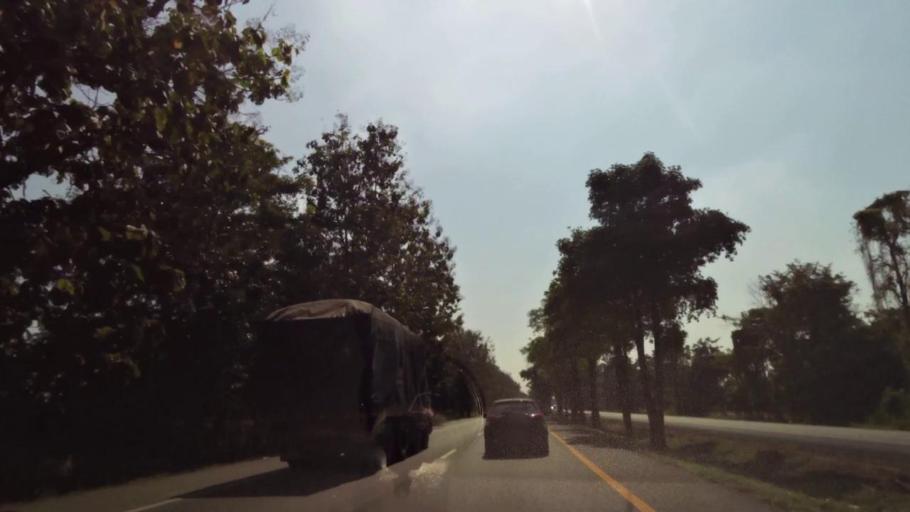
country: TH
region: Phichit
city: Bueng Na Rang
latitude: 16.0609
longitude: 100.1229
